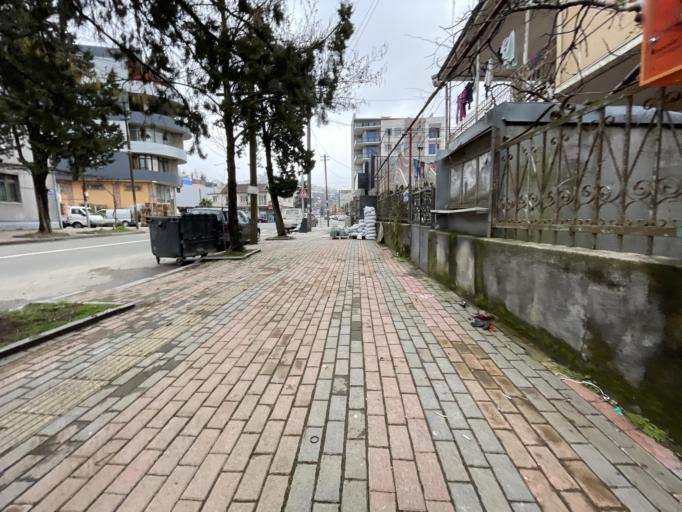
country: GE
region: Ajaria
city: Batumi
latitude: 41.6377
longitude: 41.6415
